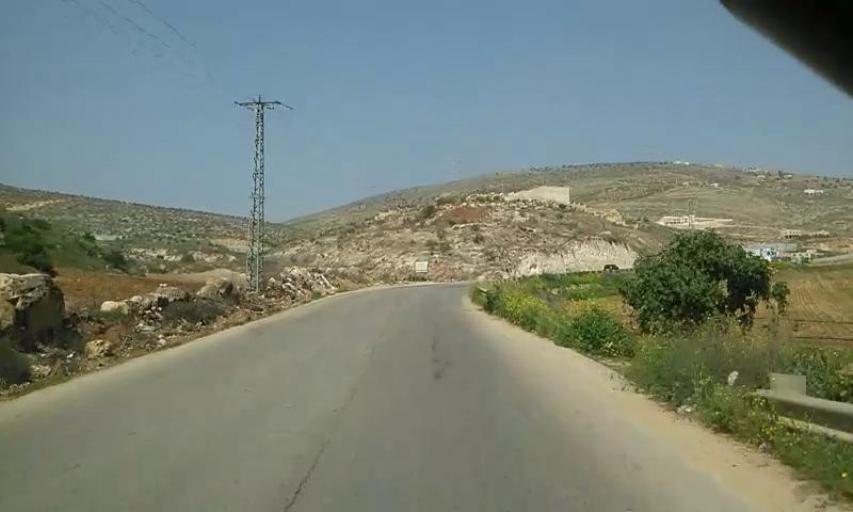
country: PS
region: West Bank
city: Tubas
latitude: 32.3017
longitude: 35.3641
